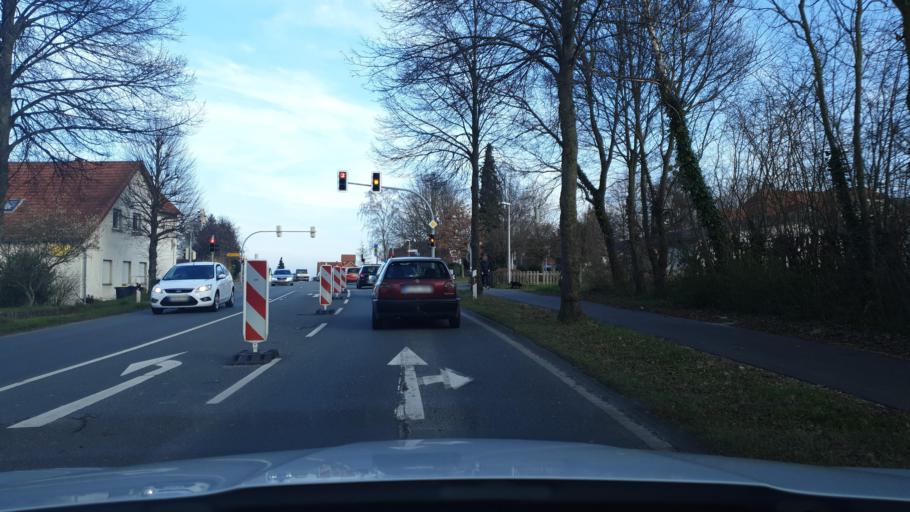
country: DE
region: North Rhine-Westphalia
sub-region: Regierungsbezirk Detmold
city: Minden
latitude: 52.2603
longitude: 8.8709
